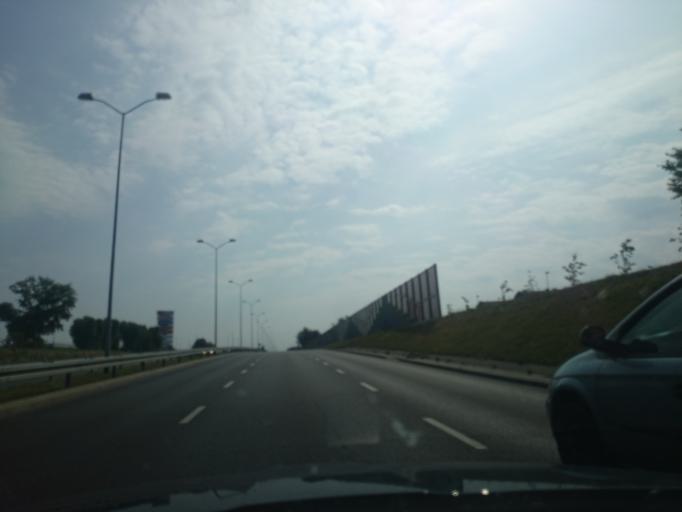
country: PL
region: West Pomeranian Voivodeship
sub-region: Szczecin
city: Szczecin
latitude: 53.3833
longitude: 14.6612
